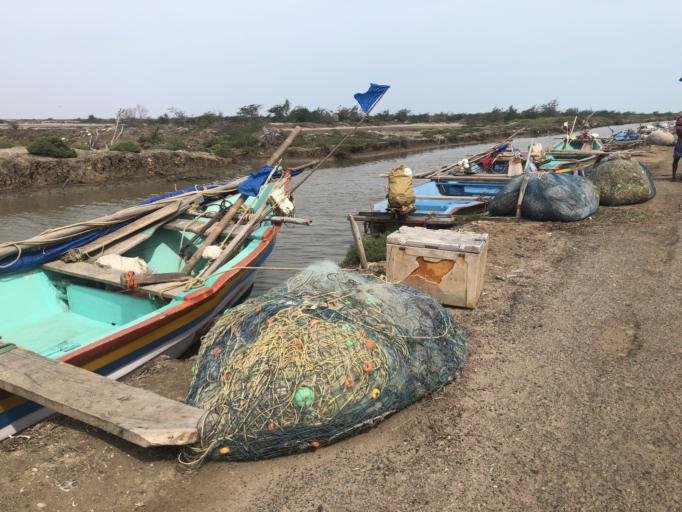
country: IN
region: Tamil Nadu
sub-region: Thanjavur
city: Adirampattinam
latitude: 10.3204
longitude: 79.3799
